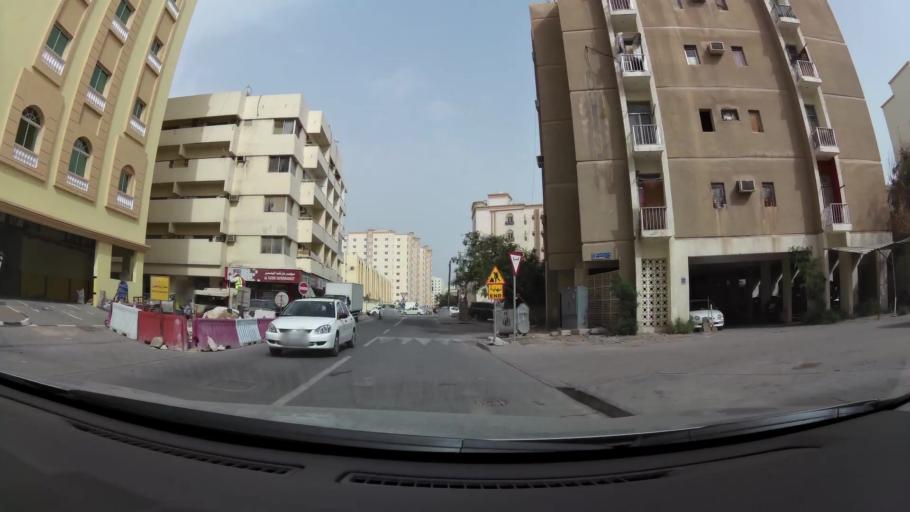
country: QA
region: Baladiyat ad Dawhah
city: Doha
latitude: 25.2757
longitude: 51.5450
